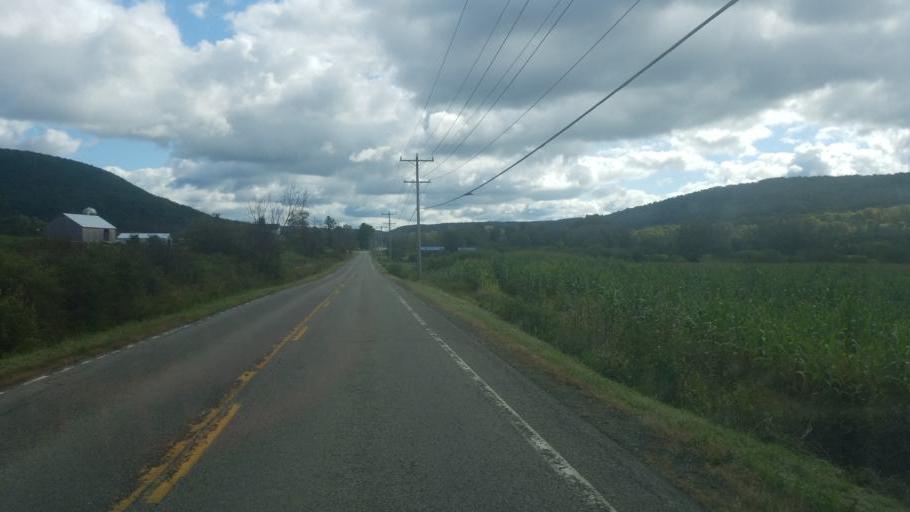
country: US
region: New York
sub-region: Allegany County
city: Cuba
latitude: 42.2178
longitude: -78.3203
